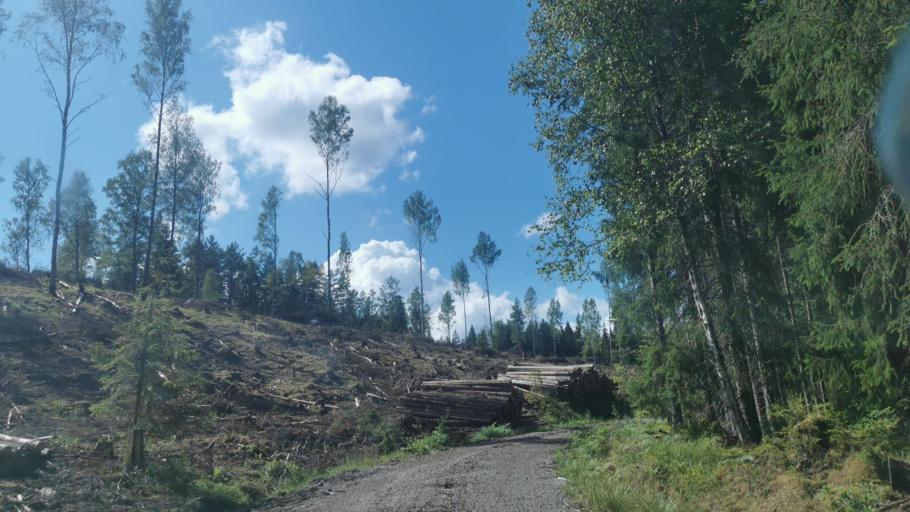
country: SE
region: OEstergoetland
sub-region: Finspangs Kommun
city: Finspang
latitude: 58.7914
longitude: 15.8357
